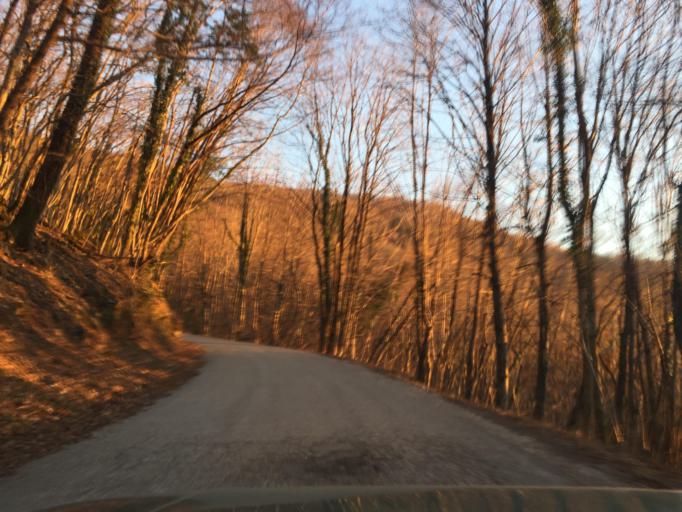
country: SI
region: Kanal
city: Kanal
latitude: 46.0756
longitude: 13.6479
